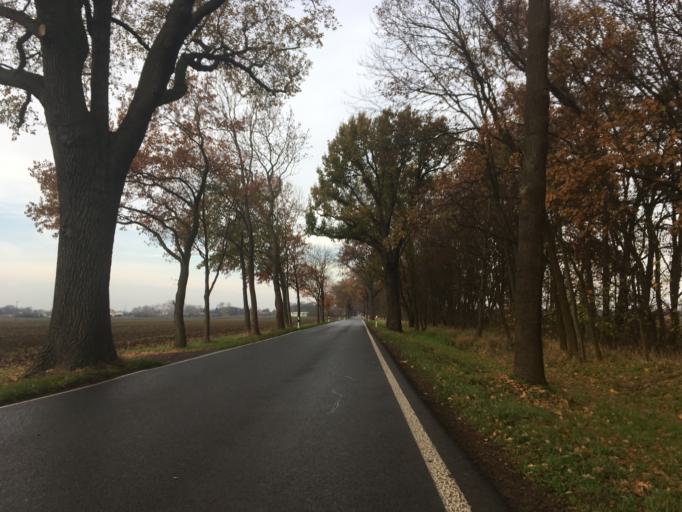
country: DE
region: Brandenburg
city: Neulewin
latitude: 52.7188
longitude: 14.2922
